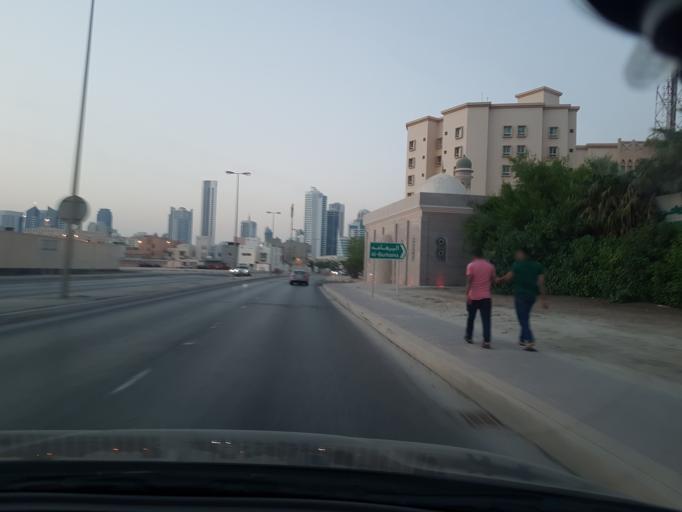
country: BH
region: Manama
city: Jidd Hafs
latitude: 26.2224
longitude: 50.5520
